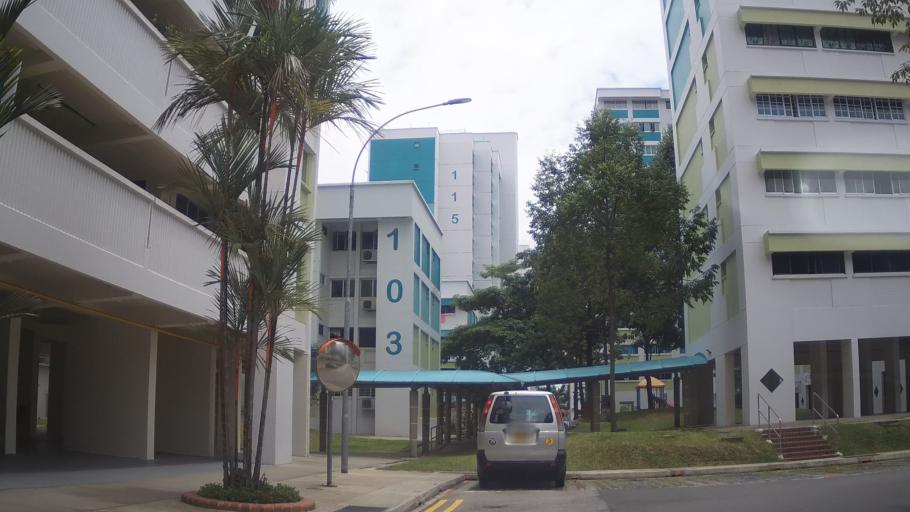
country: MY
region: Johor
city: Johor Bahru
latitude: 1.3787
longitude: 103.7680
